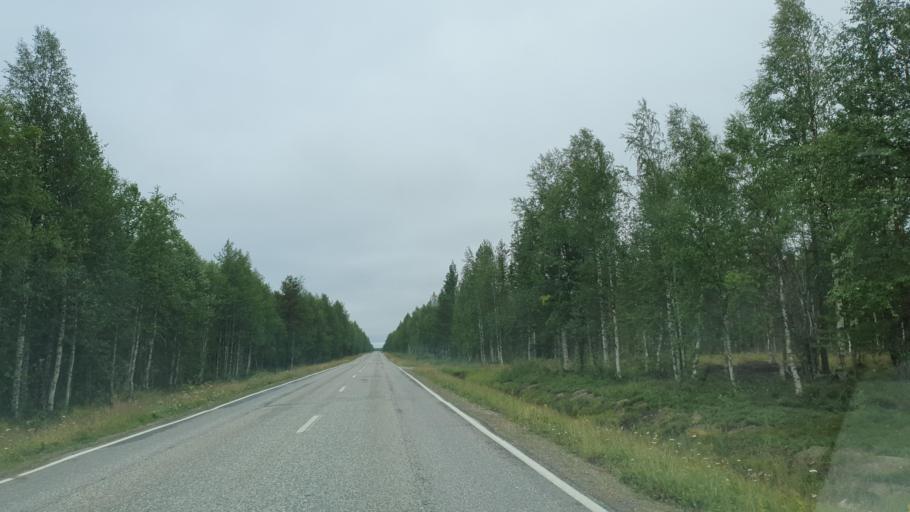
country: FI
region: Lapland
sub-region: Pohjois-Lappi
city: Sodankylae
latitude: 67.3909
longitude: 26.7713
